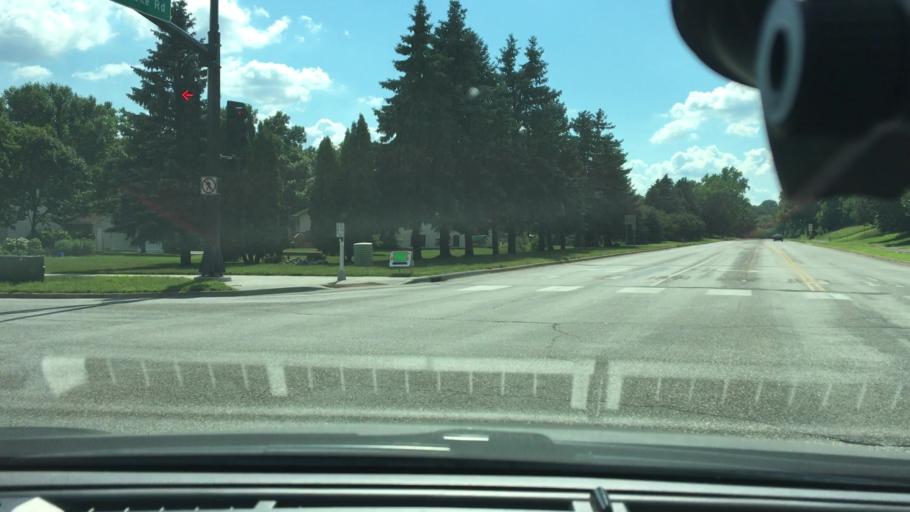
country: US
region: Minnesota
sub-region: Hennepin County
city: New Hope
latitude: 45.0438
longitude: -93.4056
